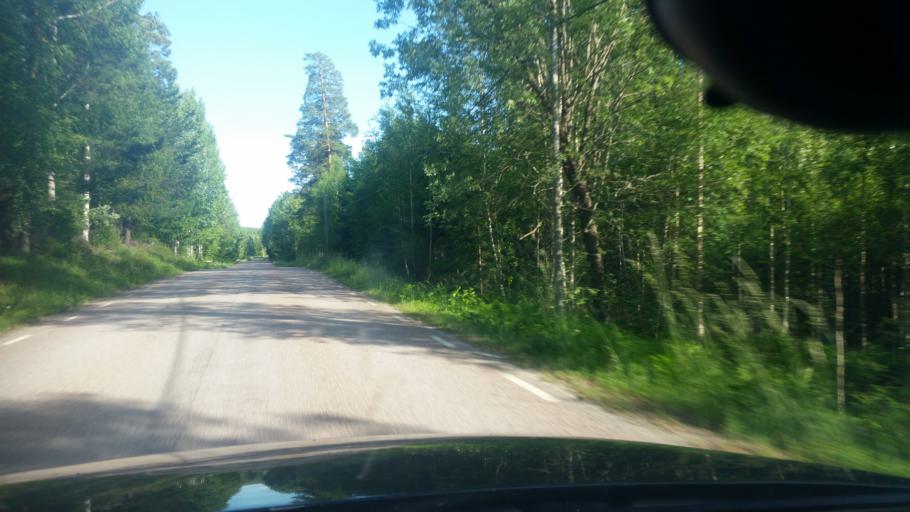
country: SE
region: Soedermanland
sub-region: Katrineholms Kommun
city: Katrineholm
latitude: 59.0762
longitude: 16.0905
